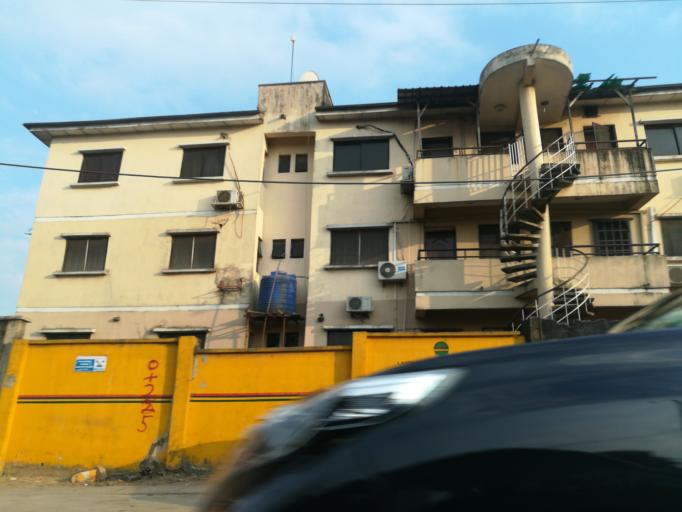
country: NG
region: Lagos
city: Ojota
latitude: 6.5855
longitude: 3.3926
